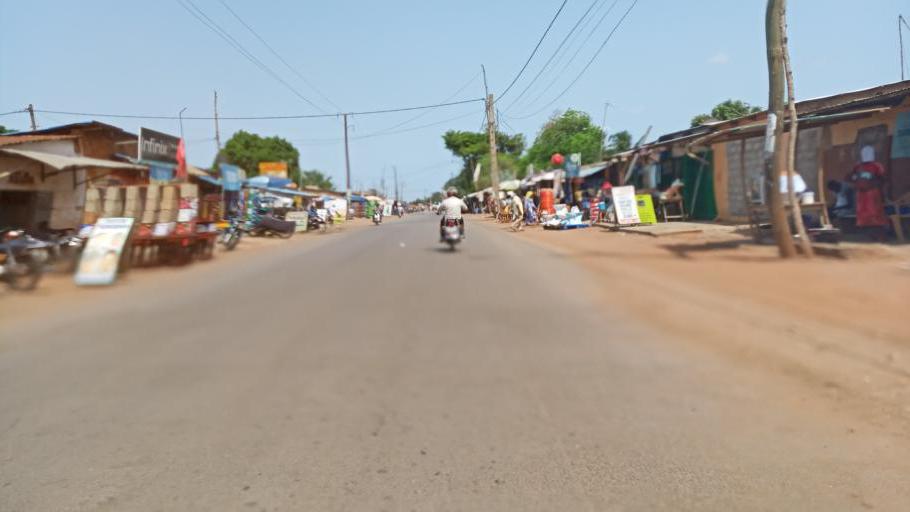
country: TG
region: Maritime
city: Lome
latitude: 6.2253
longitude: 1.2052
